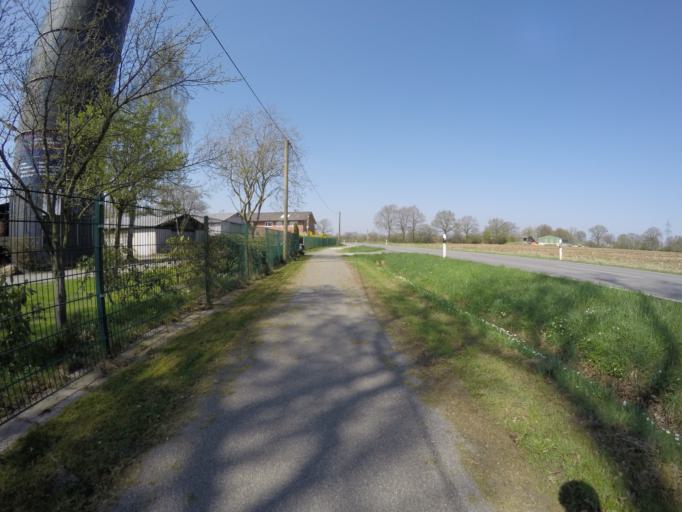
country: DE
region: Schleswig-Holstein
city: Bilsen
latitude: 53.7566
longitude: 9.8702
